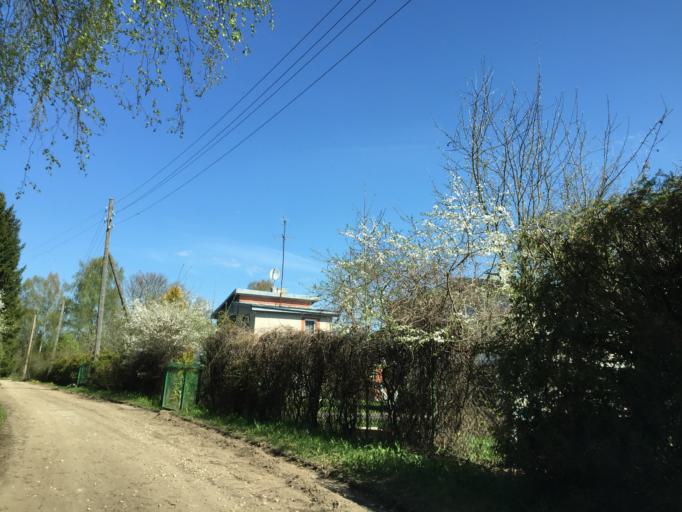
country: LV
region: Saulkrastu
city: Saulkrasti
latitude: 57.3175
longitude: 24.4363
